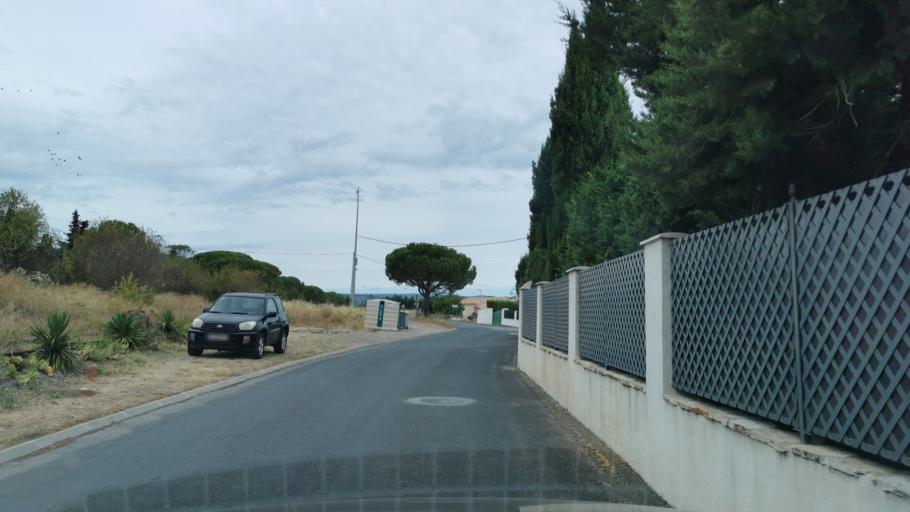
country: FR
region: Languedoc-Roussillon
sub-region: Departement de l'Aude
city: Saint-Marcel-sur-Aude
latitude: 43.2672
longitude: 2.9402
